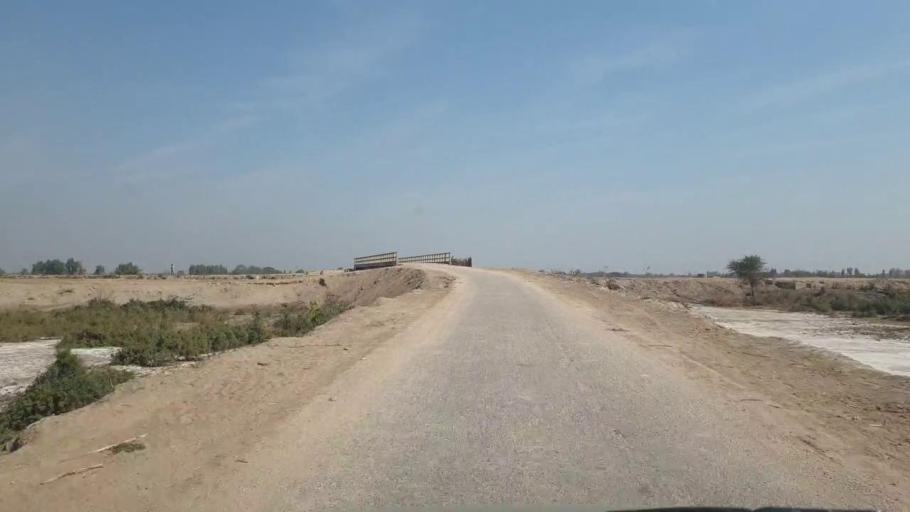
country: PK
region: Sindh
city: Chambar
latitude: 25.3829
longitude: 68.8069
